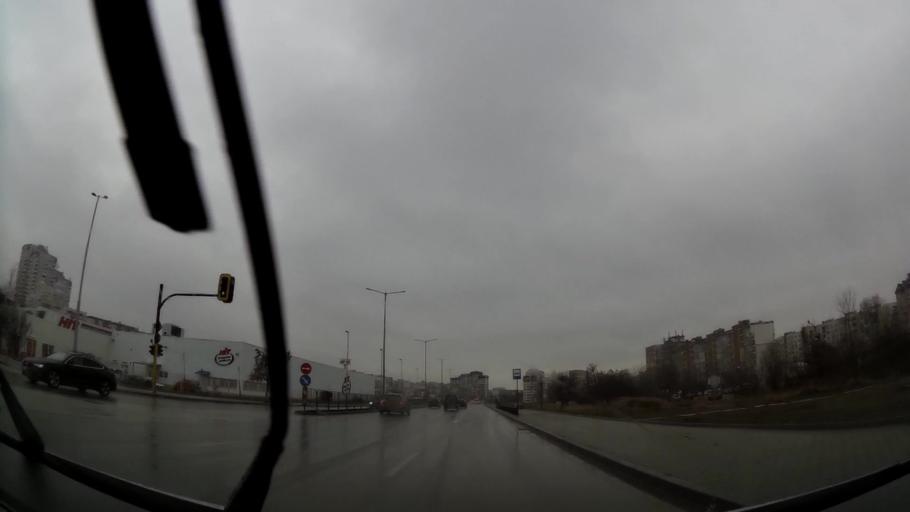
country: BG
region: Sofia-Capital
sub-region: Stolichna Obshtina
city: Sofia
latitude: 42.6373
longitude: 23.3731
